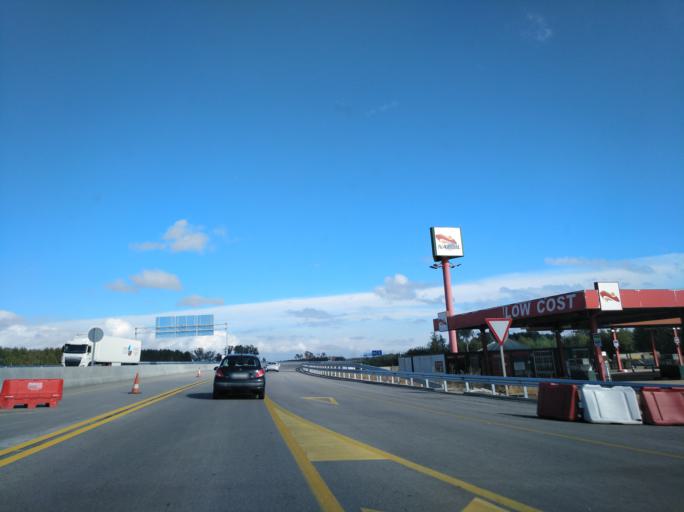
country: ES
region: Catalonia
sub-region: Provincia de Girona
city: Sils
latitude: 41.7880
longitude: 2.7571
